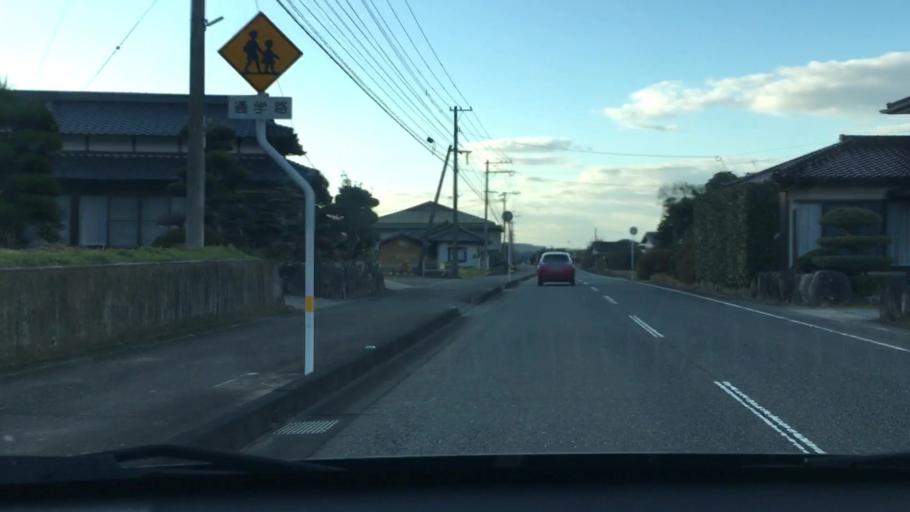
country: JP
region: Oita
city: Bungo-Takada-shi
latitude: 33.5017
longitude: 131.3729
